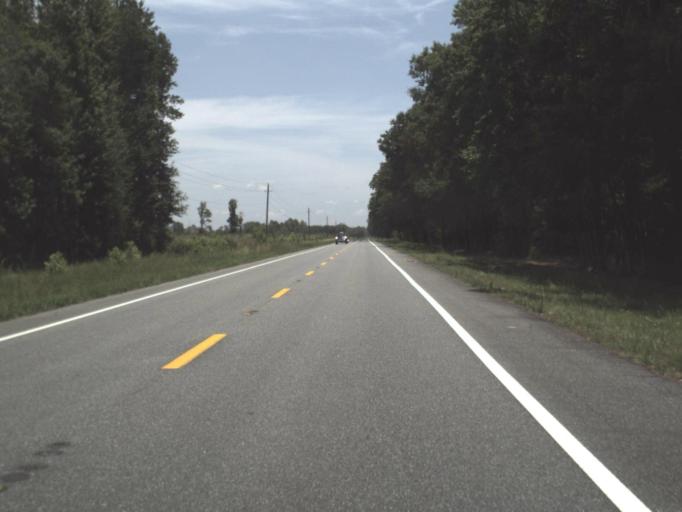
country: US
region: Florida
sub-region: Lafayette County
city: Mayo
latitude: 29.9678
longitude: -83.2207
